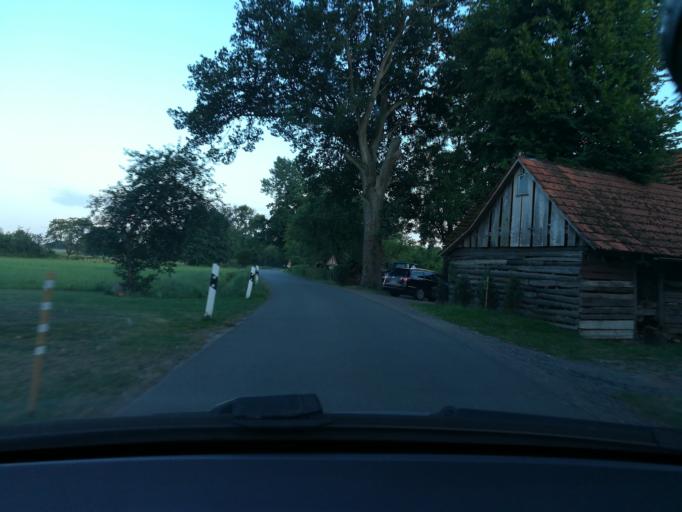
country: DE
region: North Rhine-Westphalia
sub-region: Regierungsbezirk Munster
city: Lienen
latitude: 52.1433
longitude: 7.9849
